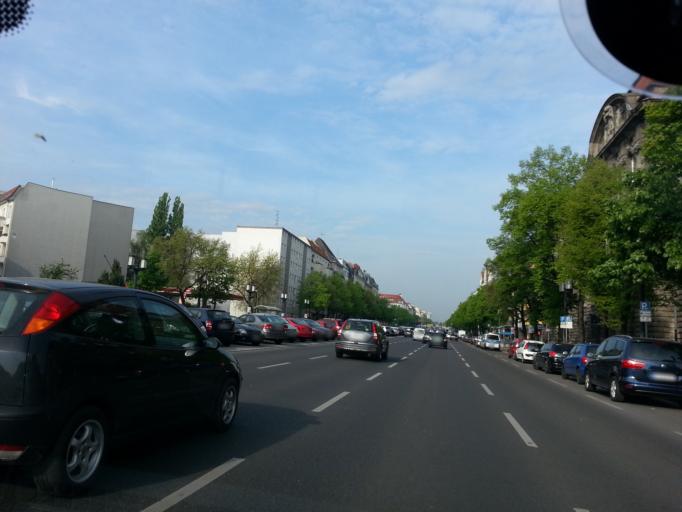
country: DE
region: Berlin
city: Charlottenburg Bezirk
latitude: 52.5110
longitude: 13.2963
